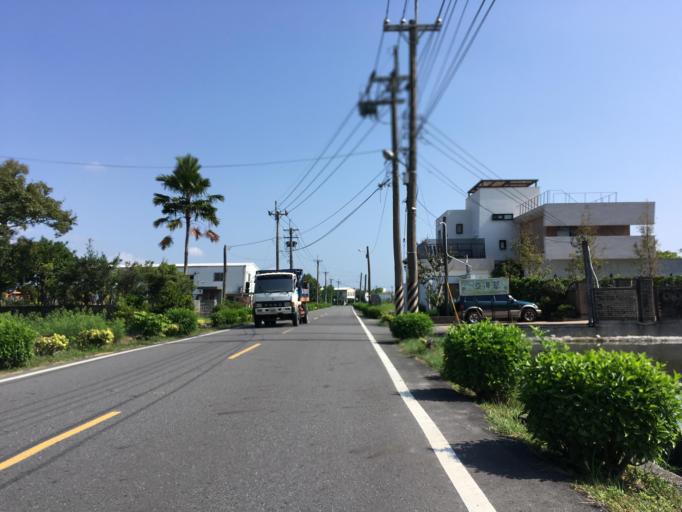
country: TW
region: Taiwan
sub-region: Yilan
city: Yilan
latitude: 24.6770
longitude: 121.7339
